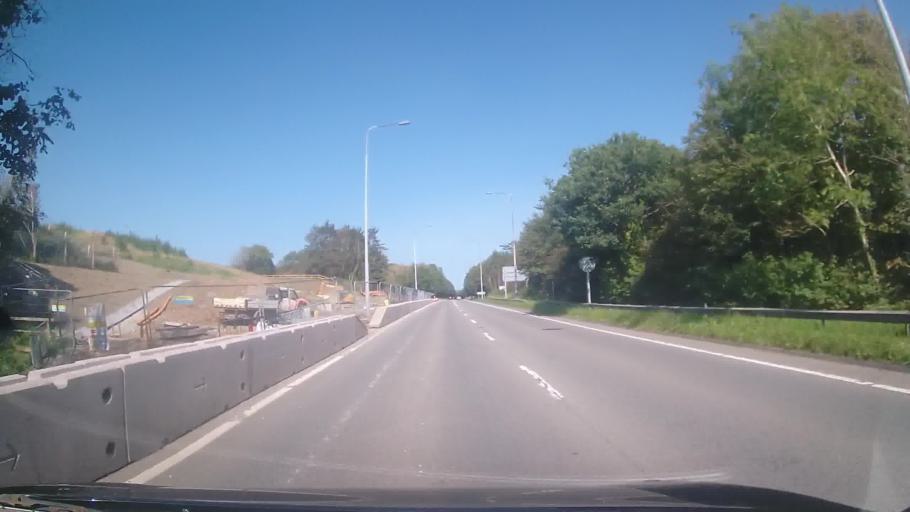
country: GB
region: Wales
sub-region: Pembrokeshire
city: Haverfordwest
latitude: 51.8052
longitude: -4.9579
